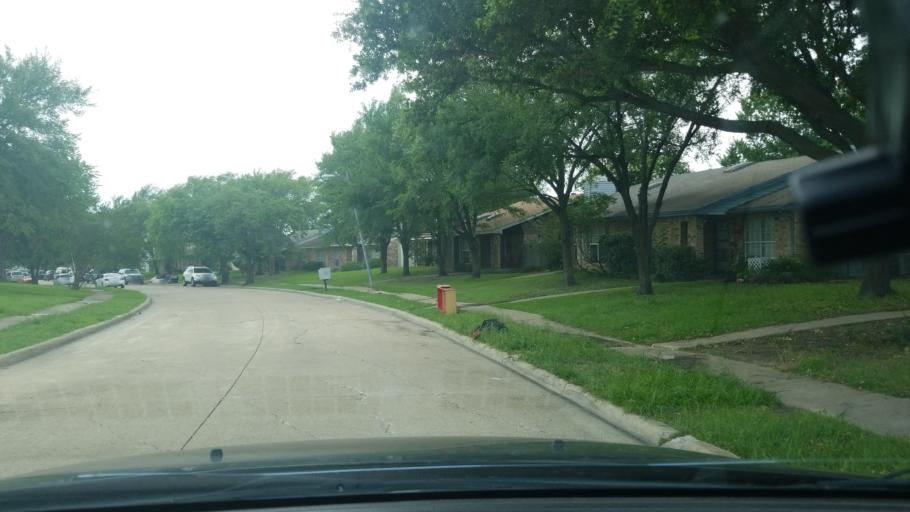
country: US
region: Texas
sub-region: Dallas County
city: Mesquite
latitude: 32.7995
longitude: -96.6170
